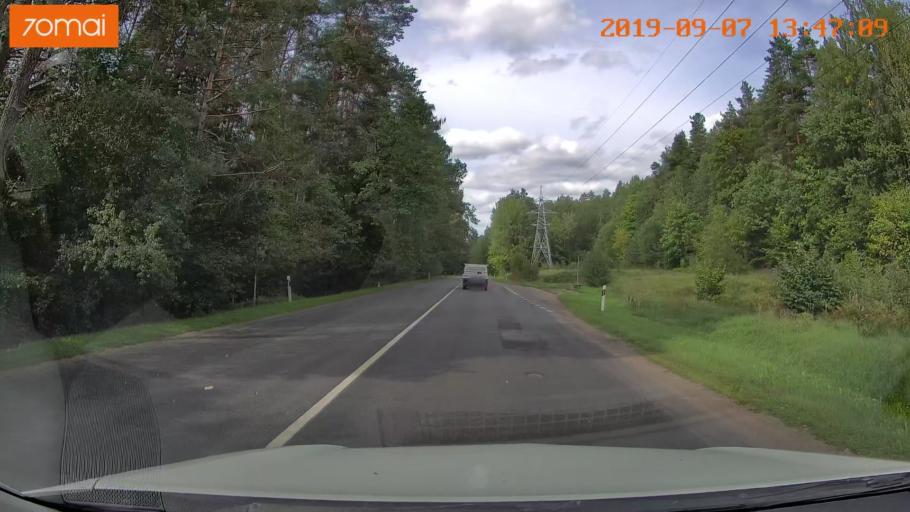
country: LT
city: Baltoji Voke
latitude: 54.5951
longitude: 25.2180
